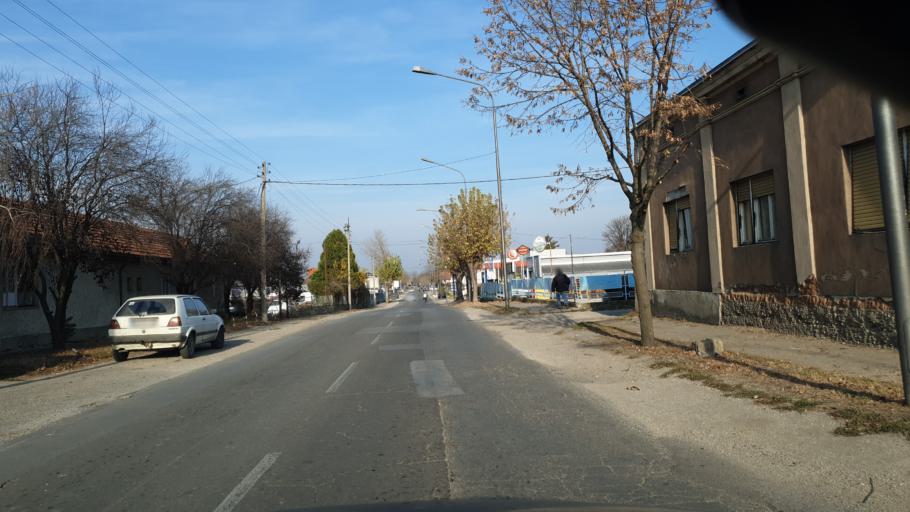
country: RS
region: Central Serbia
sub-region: Zajecarski Okrug
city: Zajecar
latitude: 43.9077
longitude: 22.2876
